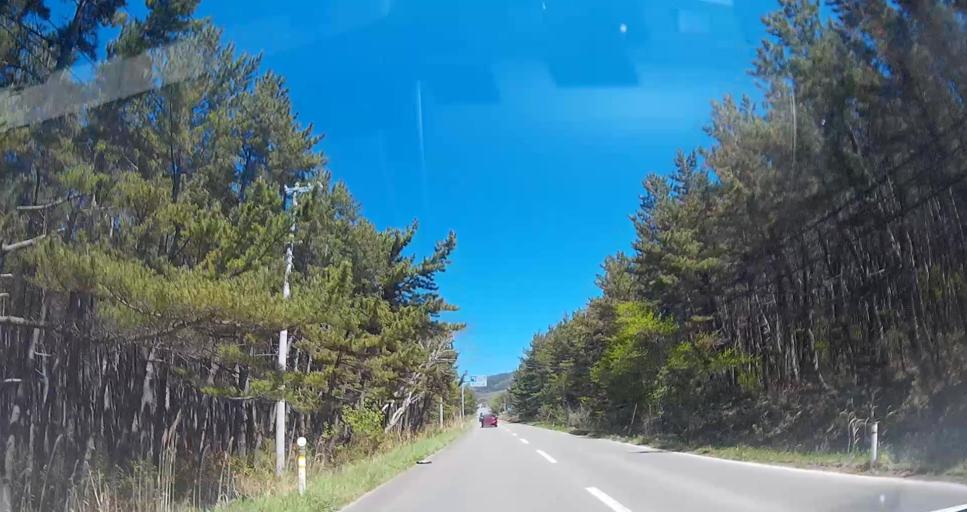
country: JP
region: Aomori
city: Mutsu
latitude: 41.3766
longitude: 141.3932
